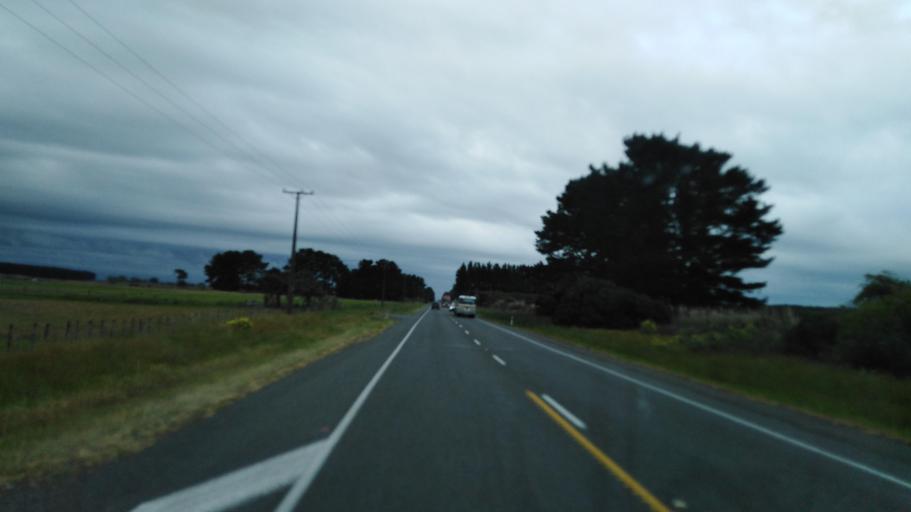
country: NZ
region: Manawatu-Wanganui
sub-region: Horowhenua District
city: Foxton
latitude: -40.4067
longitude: 175.3098
